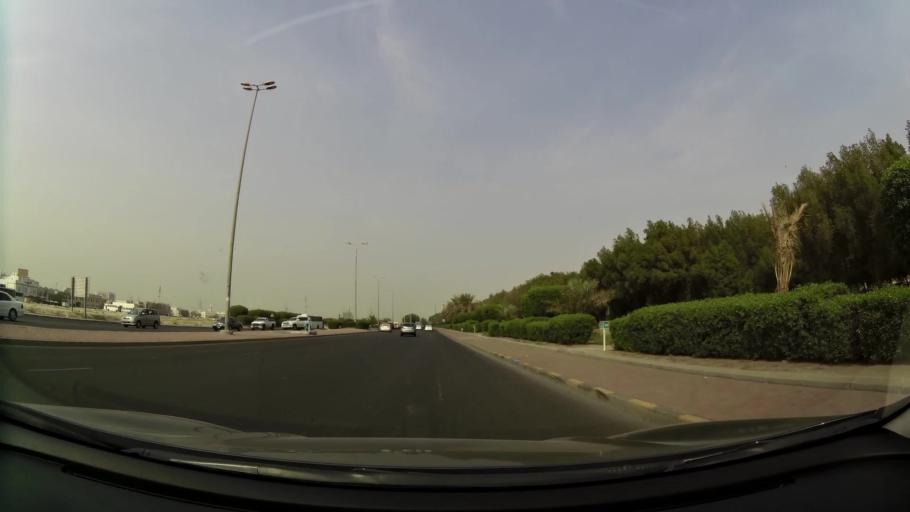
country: KW
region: Al Asimah
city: Ar Rabiyah
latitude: 29.2897
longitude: 47.9284
